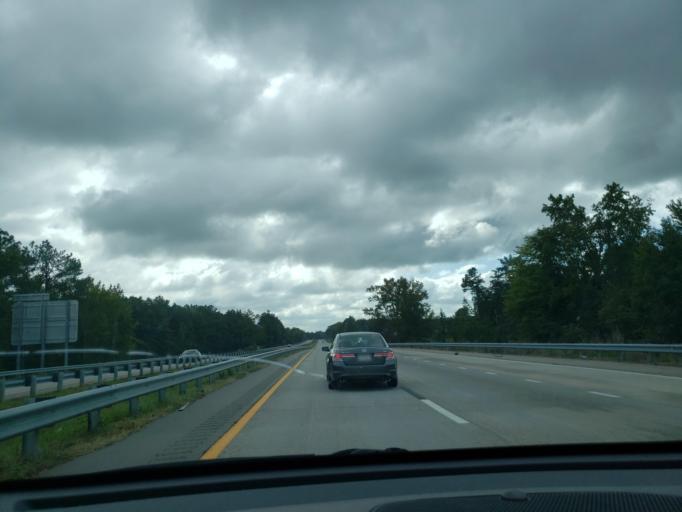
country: US
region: North Carolina
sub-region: Vance County
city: Henderson
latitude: 36.3926
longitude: -78.3391
